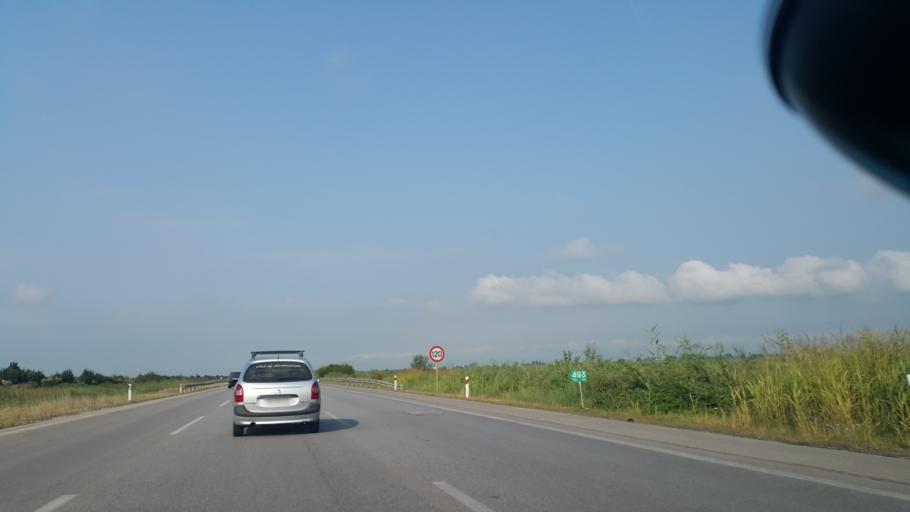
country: GR
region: Central Macedonia
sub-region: Nomos Thessalonikis
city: Sindos
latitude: 40.6391
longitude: 22.7915
